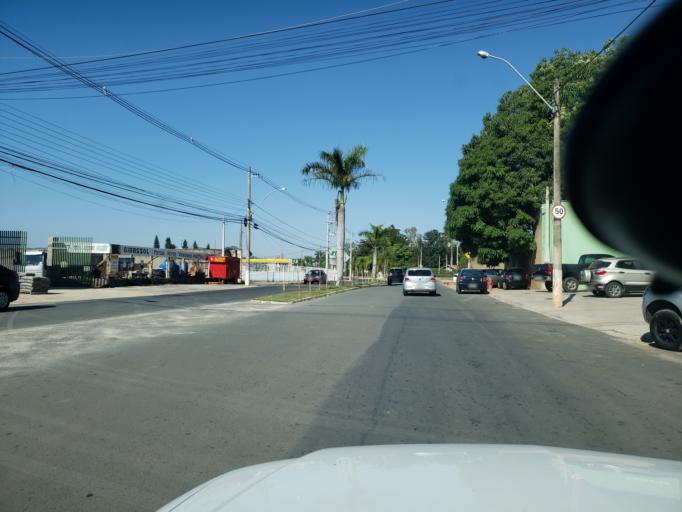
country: BR
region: Sao Paulo
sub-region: Itapira
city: Itapira
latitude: -22.4197
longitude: -46.8388
